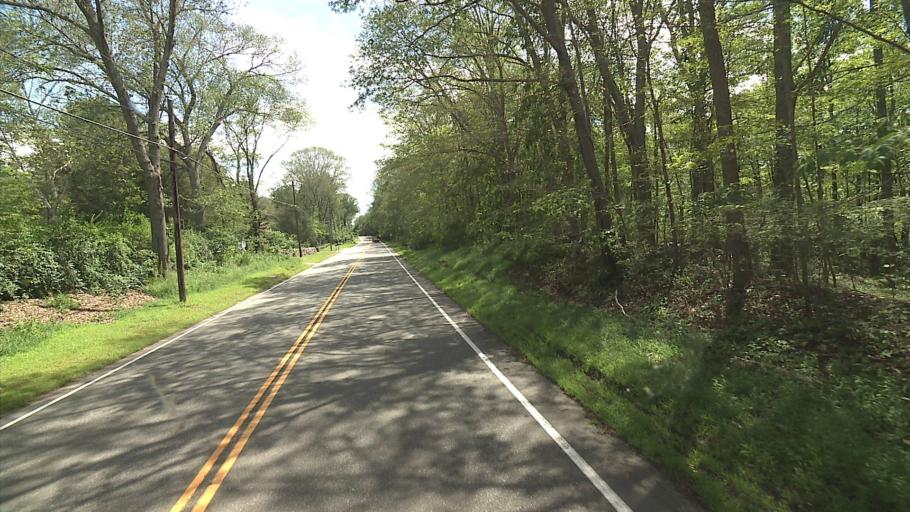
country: US
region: Connecticut
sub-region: Tolland County
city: Mansfield City
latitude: 41.7794
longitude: -72.2122
